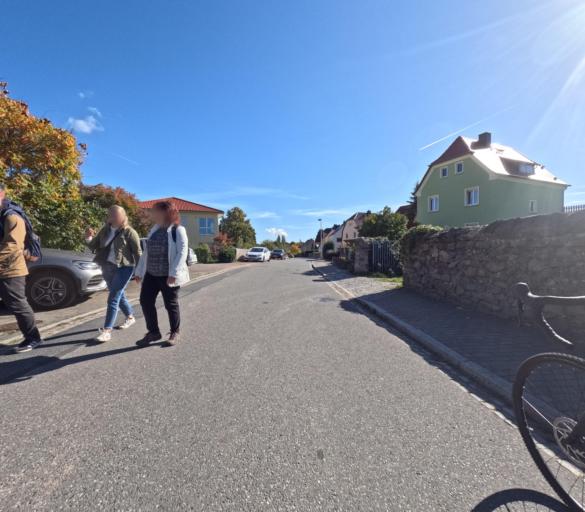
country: DE
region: Saxony
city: Radebeul
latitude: 51.1163
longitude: 13.6785
